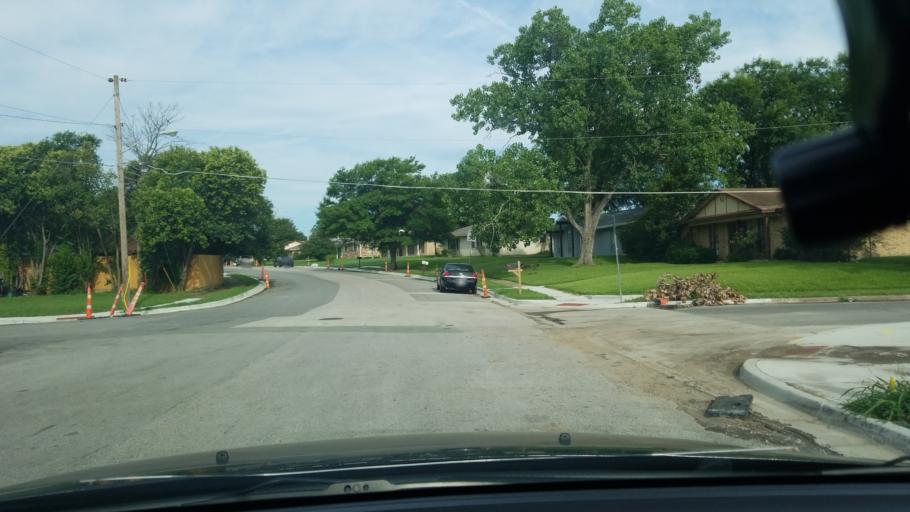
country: US
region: Texas
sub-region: Dallas County
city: Balch Springs
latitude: 32.7570
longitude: -96.6542
